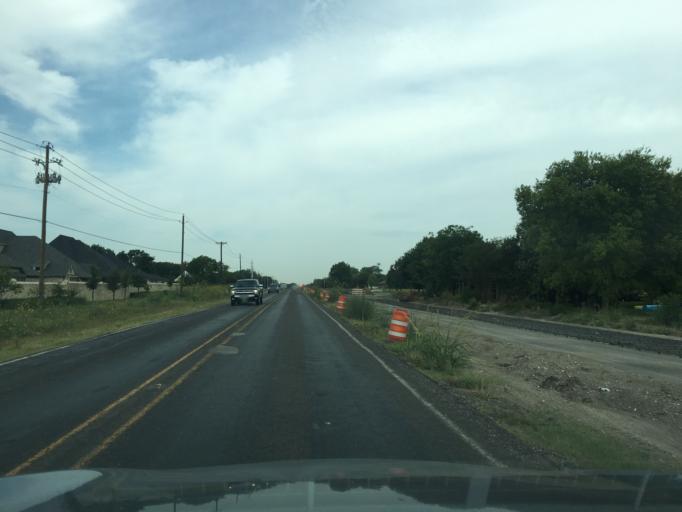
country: US
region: Texas
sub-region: Collin County
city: Lucas
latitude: 33.0550
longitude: -96.5801
